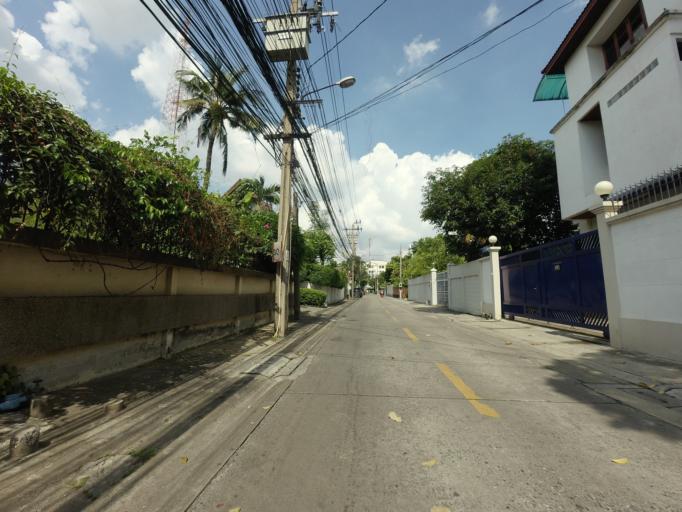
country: TH
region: Bangkok
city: Phaya Thai
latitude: 13.7825
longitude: 100.5519
